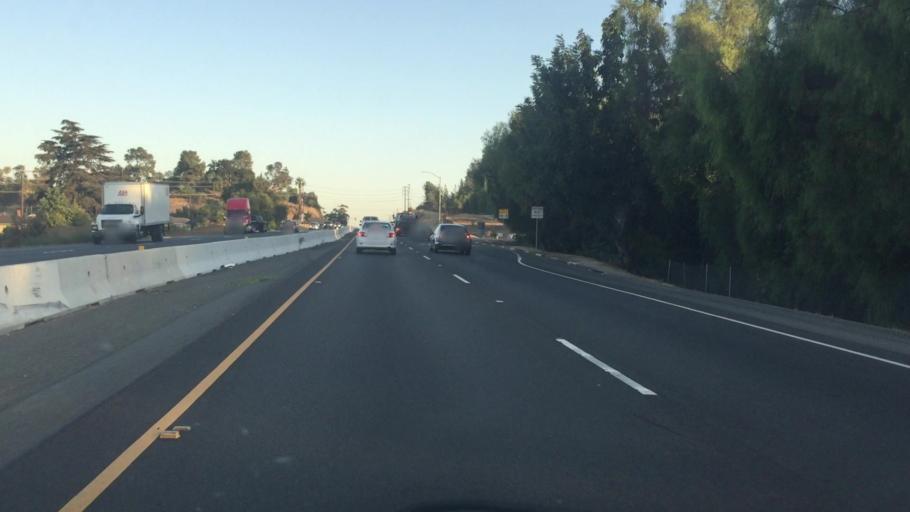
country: US
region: California
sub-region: Los Angeles County
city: Pomona
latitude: 34.0472
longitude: -117.7747
